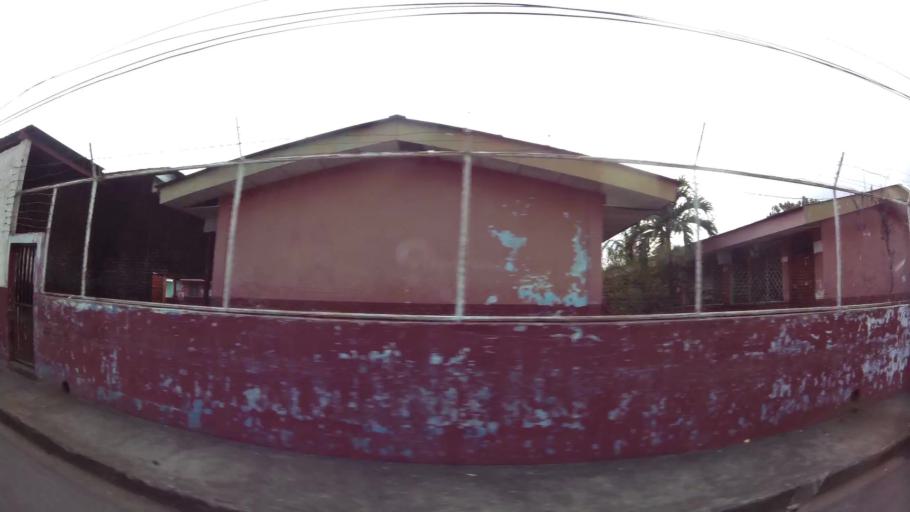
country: NI
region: Masaya
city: Masaya
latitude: 11.9791
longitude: -86.0990
